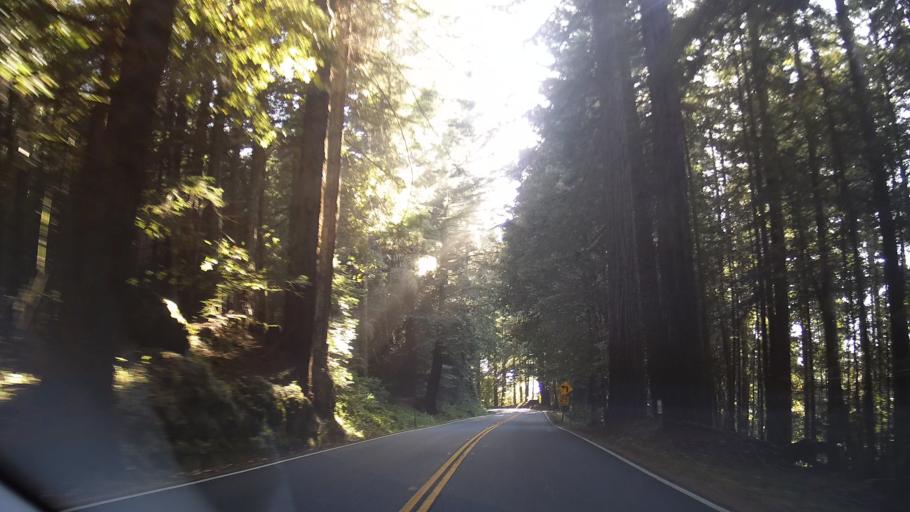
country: US
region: California
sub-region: Mendocino County
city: Fort Bragg
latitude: 39.3590
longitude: -123.6222
